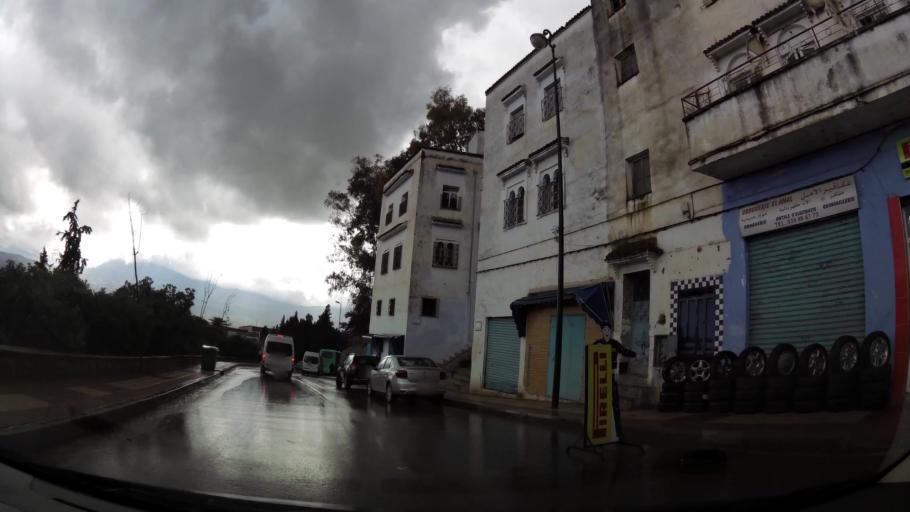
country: MA
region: Tanger-Tetouan
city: Chefchaouene
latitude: 35.1706
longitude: -5.2699
